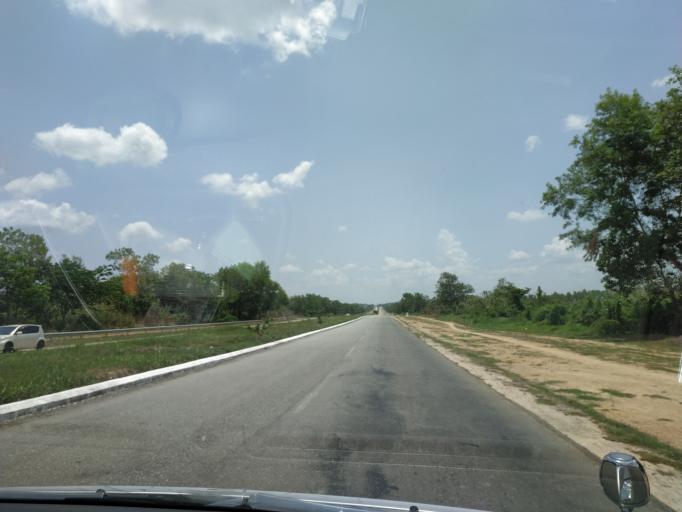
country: MM
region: Bago
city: Thanatpin
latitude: 17.3564
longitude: 96.2543
